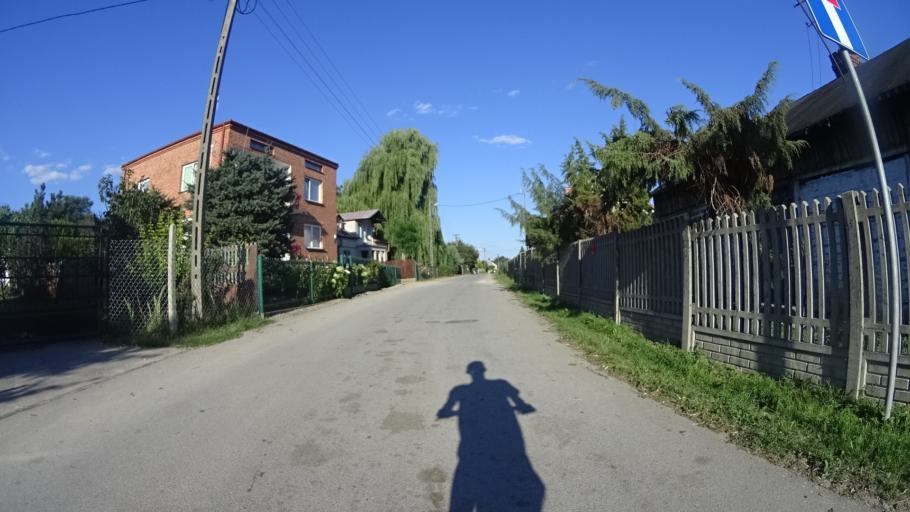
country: PL
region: Masovian Voivodeship
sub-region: Powiat bialobrzeski
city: Wysmierzyce
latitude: 51.6568
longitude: 20.7832
